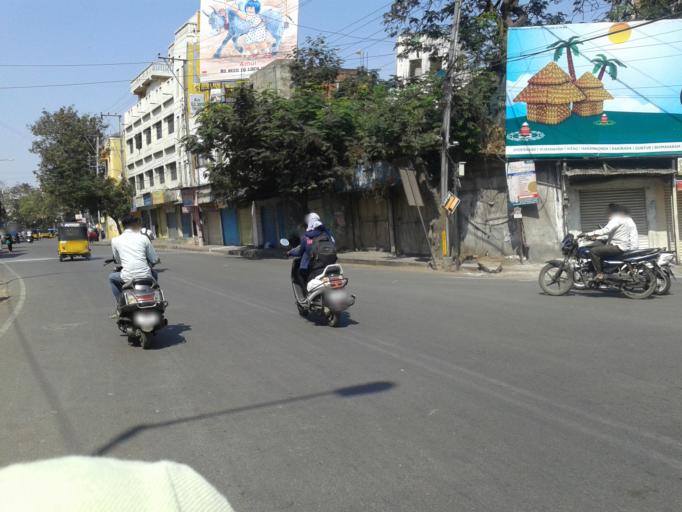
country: IN
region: Telangana
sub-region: Hyderabad
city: Hyderabad
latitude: 17.3893
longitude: 78.4858
